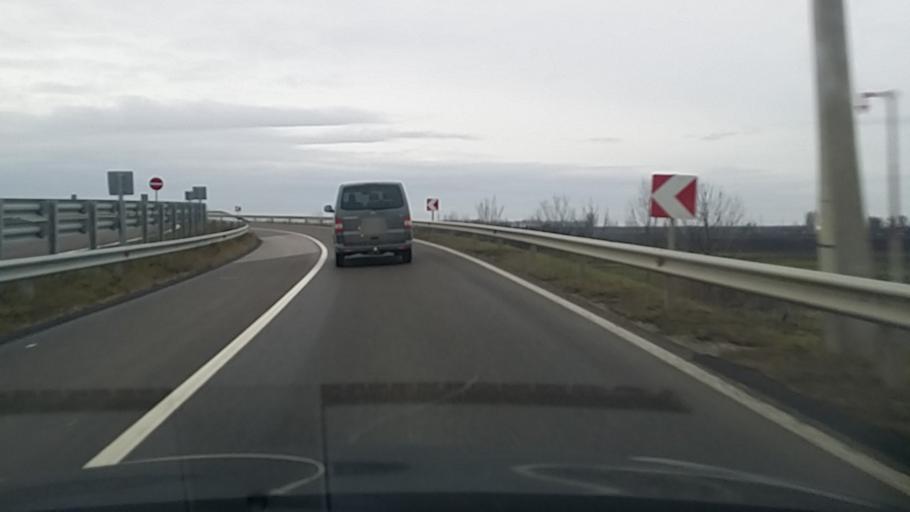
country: HU
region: Hajdu-Bihar
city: Debrecen
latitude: 47.5501
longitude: 21.5541
